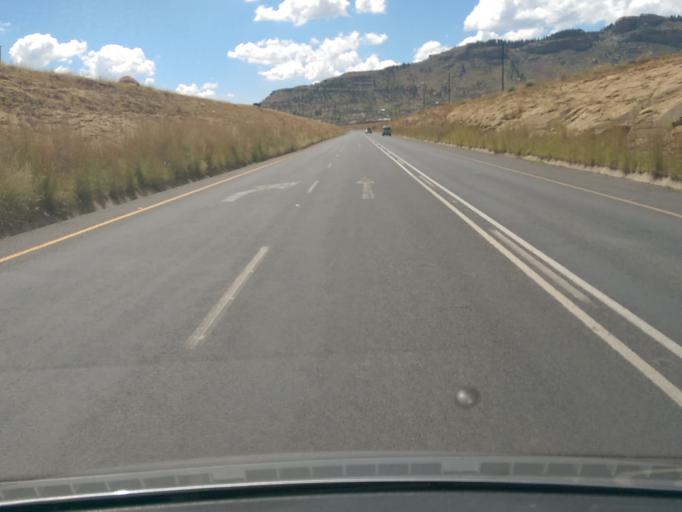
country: LS
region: Maseru
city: Maseru
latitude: -29.3735
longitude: 27.4754
